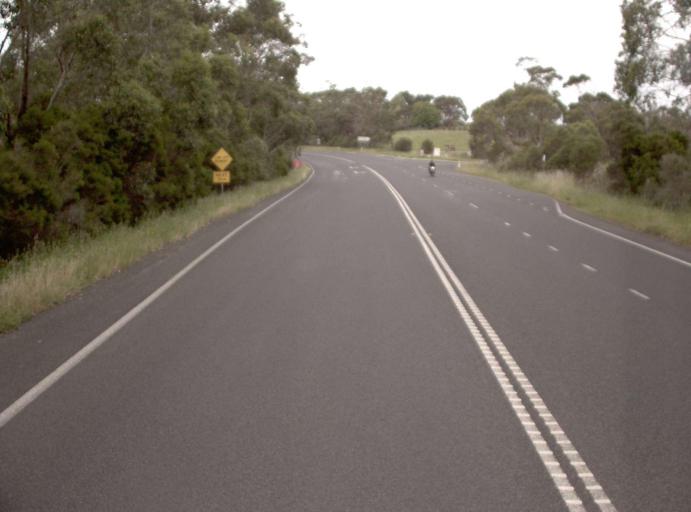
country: AU
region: Victoria
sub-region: Cardinia
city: Koo-Wee-Rup
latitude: -38.3520
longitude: 145.6489
